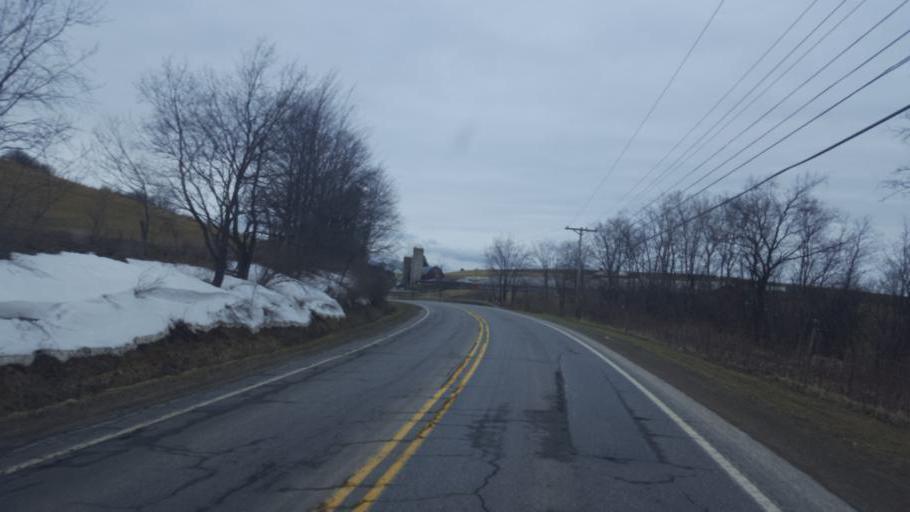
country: US
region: Pennsylvania
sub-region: Potter County
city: Coudersport
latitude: 41.8404
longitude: -77.8898
